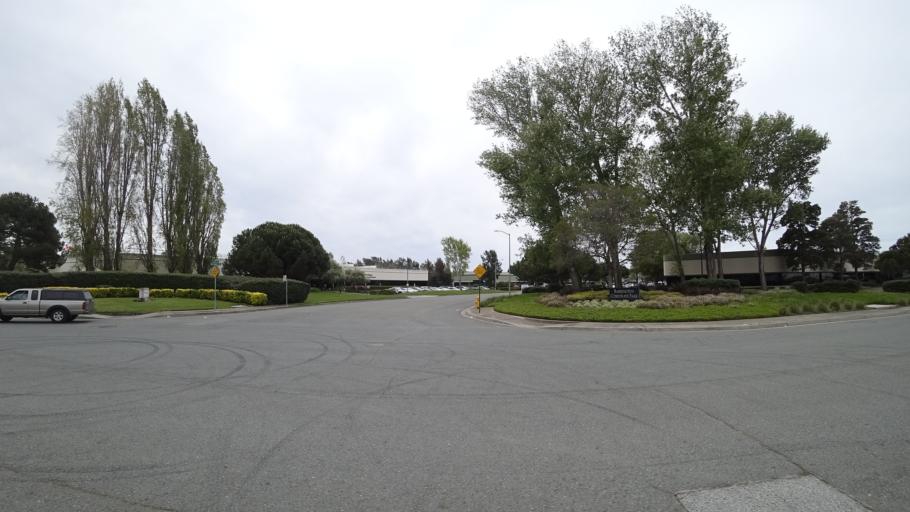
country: US
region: California
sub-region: Alameda County
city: San Lorenzo
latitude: 37.6560
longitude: -122.1400
